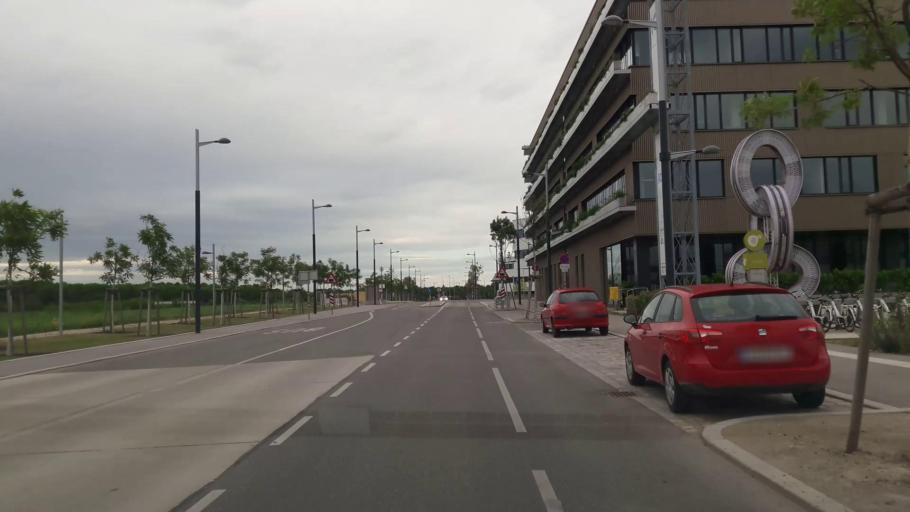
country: AT
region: Lower Austria
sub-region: Politischer Bezirk Ganserndorf
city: Gross-Enzersdorf
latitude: 48.2238
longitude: 16.5094
